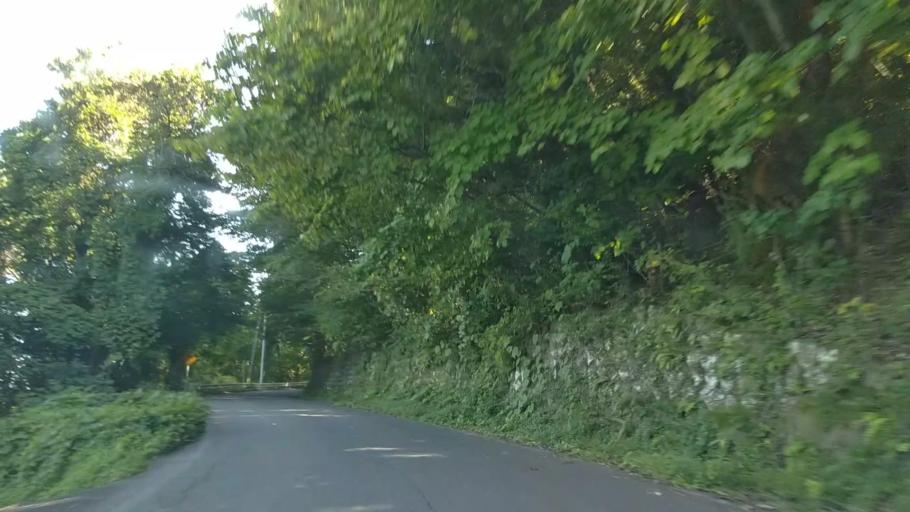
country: JP
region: Nagano
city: Nagano-shi
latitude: 36.5822
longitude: 138.0990
